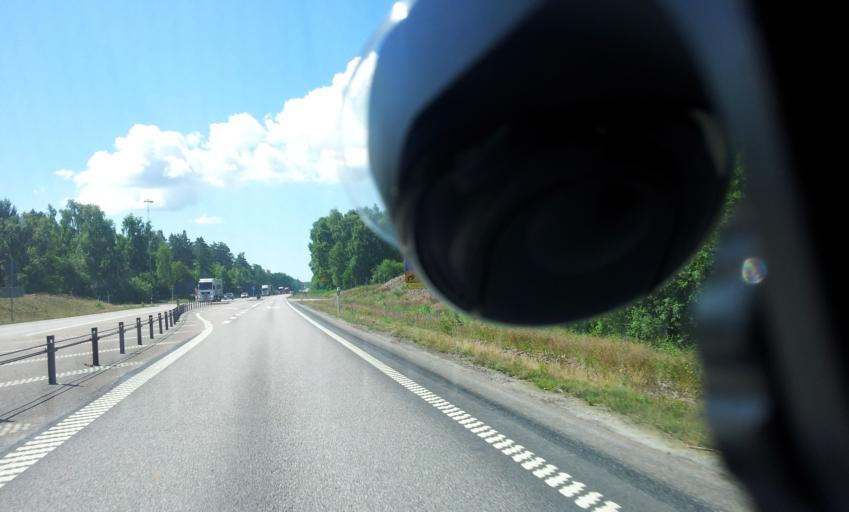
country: SE
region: Kalmar
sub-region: Oskarshamns Kommun
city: Paskallavik
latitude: 57.1801
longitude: 16.4444
